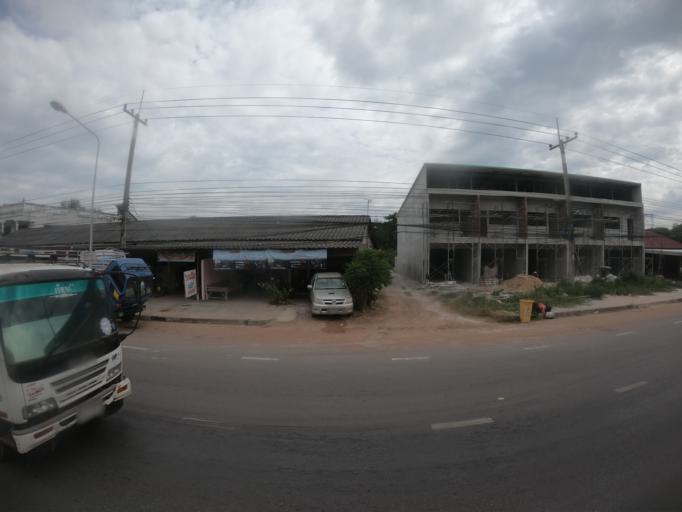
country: TH
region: Maha Sarakham
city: Kantharawichai
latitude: 16.3192
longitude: 103.2992
